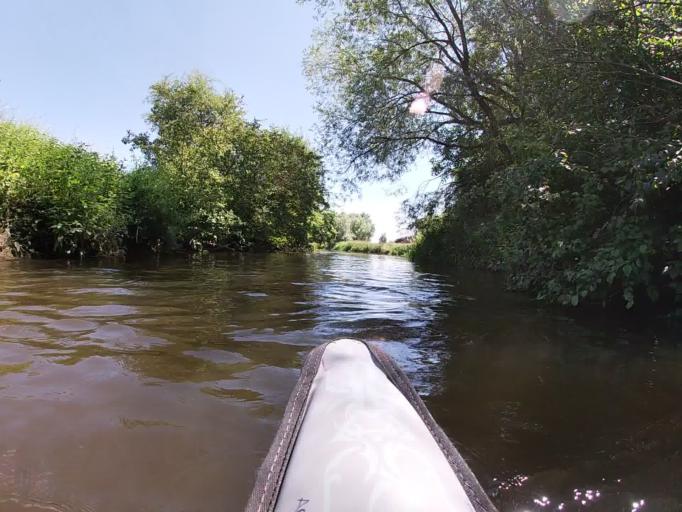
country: DE
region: Bavaria
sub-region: Upper Bavaria
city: Ramerberg
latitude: 48.0213
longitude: 12.1572
